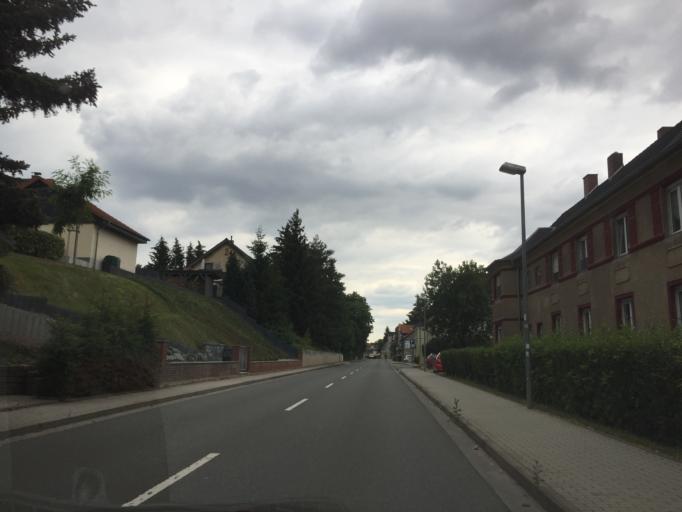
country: DE
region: Thuringia
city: Gossnitz
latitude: 50.8948
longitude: 12.4347
